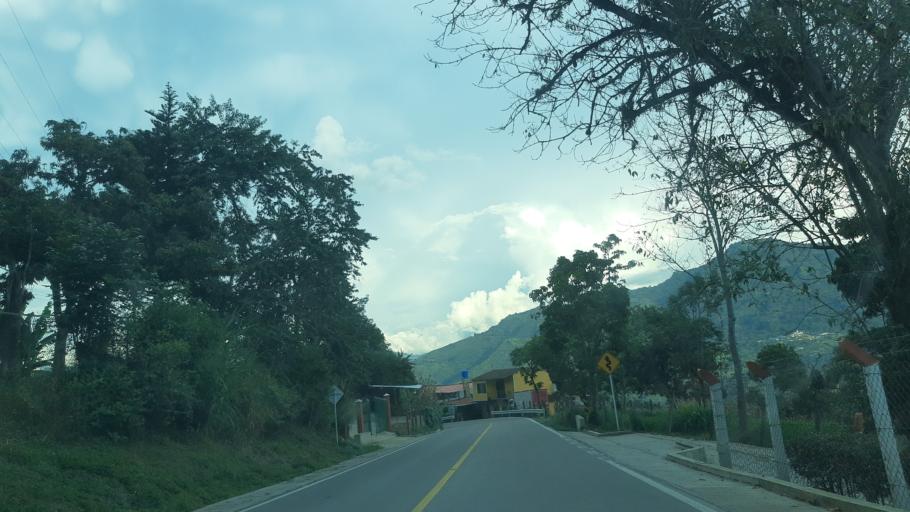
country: CO
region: Boyaca
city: Guateque
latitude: 5.0099
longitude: -73.4616
